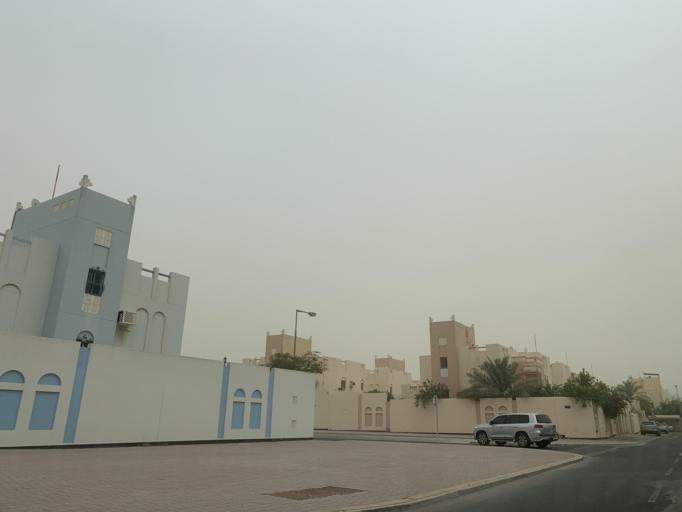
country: BH
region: Central Governorate
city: Madinat Hamad
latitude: 26.1362
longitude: 50.5121
